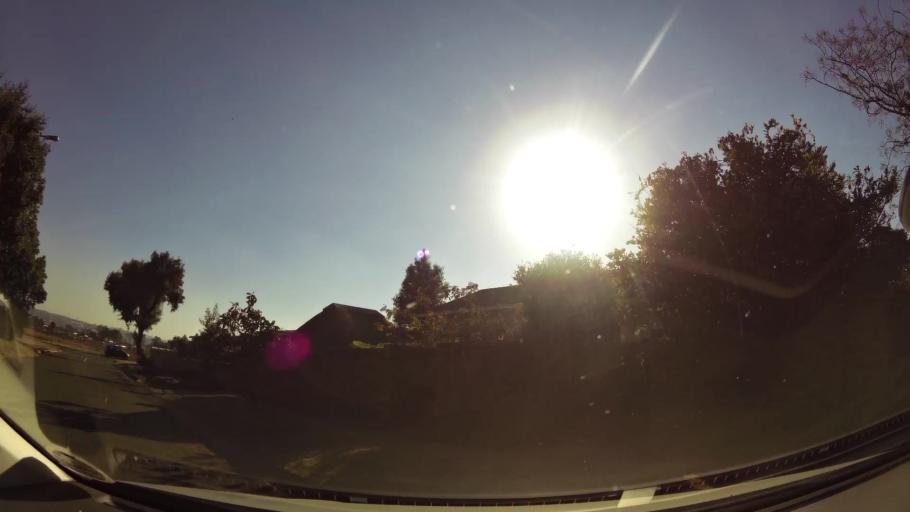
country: ZA
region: Gauteng
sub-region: City of Johannesburg Metropolitan Municipality
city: Johannesburg
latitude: -26.2060
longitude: 27.9623
